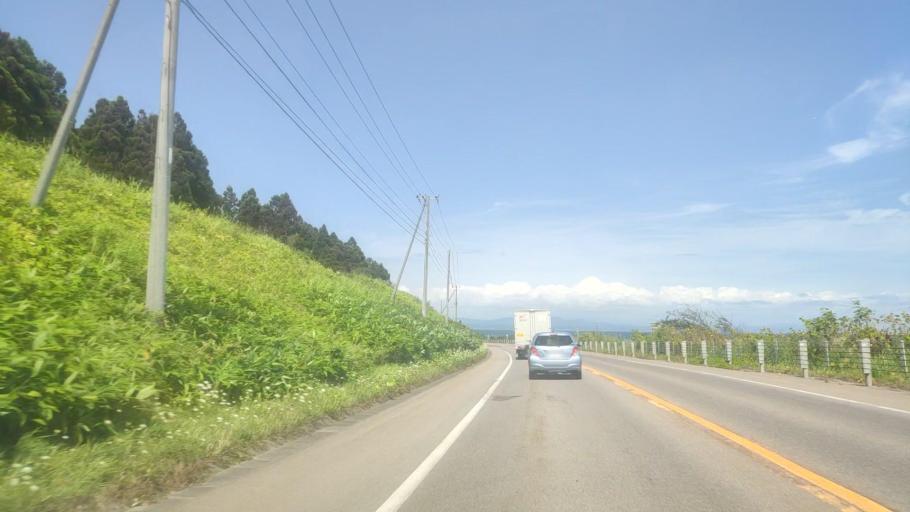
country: JP
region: Hokkaido
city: Nanae
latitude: 42.2053
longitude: 140.4055
